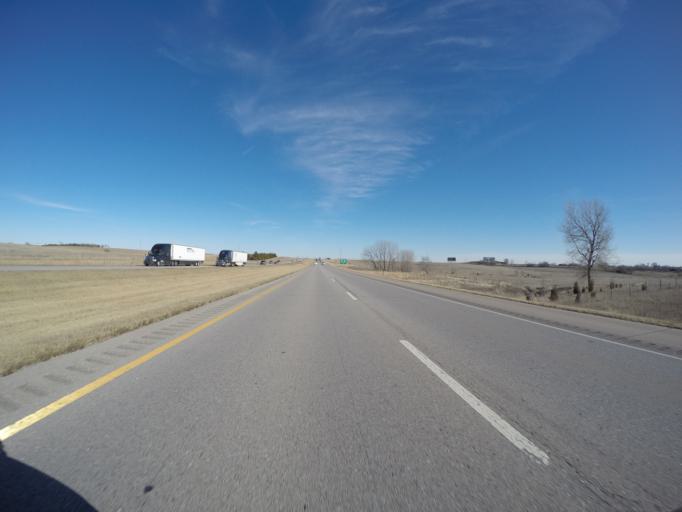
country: US
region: Nebraska
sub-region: Lancaster County
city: Lincoln
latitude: 40.8202
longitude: -96.8130
